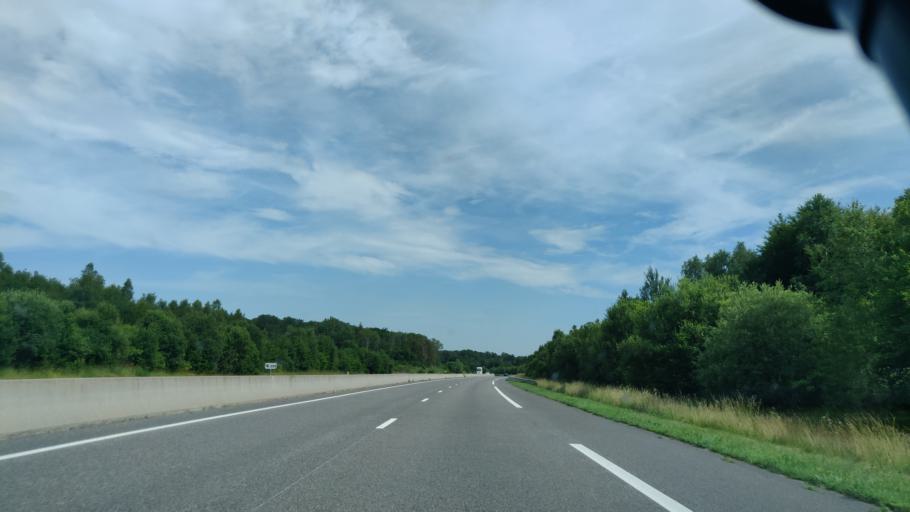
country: FR
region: Lorraine
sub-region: Departement de Meurthe-et-Moselle
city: Baccarat
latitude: 48.5091
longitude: 6.6692
